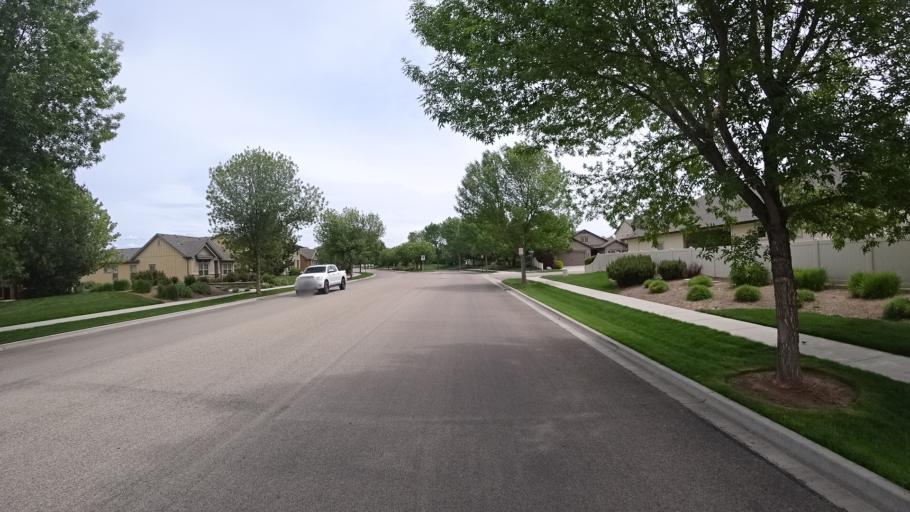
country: US
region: Idaho
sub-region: Ada County
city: Meridian
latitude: 43.5661
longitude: -116.3596
